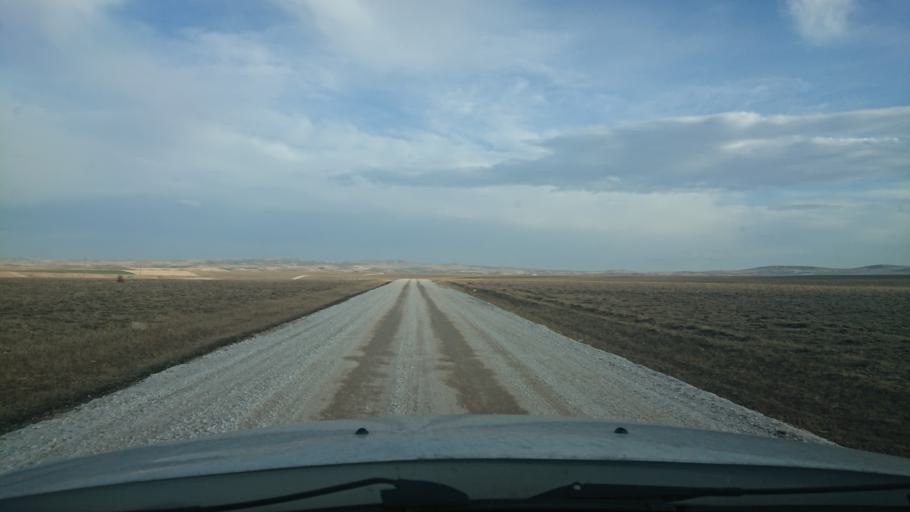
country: TR
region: Aksaray
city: Agacoren
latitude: 38.7264
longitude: 33.8680
